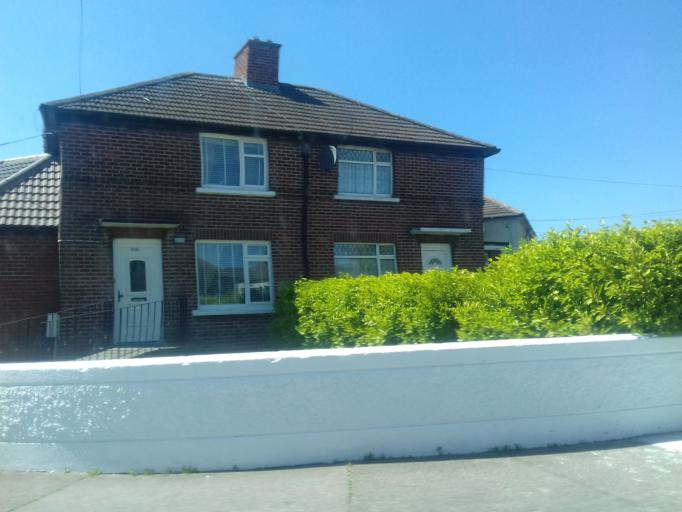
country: IE
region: Leinster
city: Cabra
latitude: 53.3676
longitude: -6.2902
